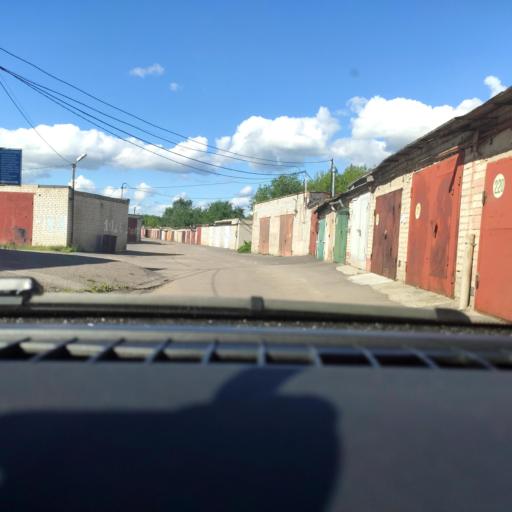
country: RU
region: Voronezj
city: Voronezh
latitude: 51.6638
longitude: 39.2912
